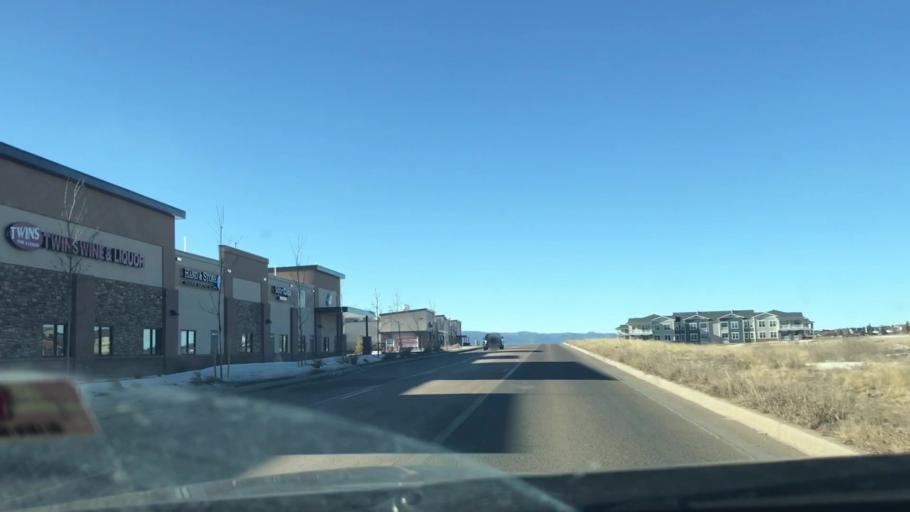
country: US
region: Colorado
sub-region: El Paso County
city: Black Forest
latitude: 38.9713
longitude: -104.7418
